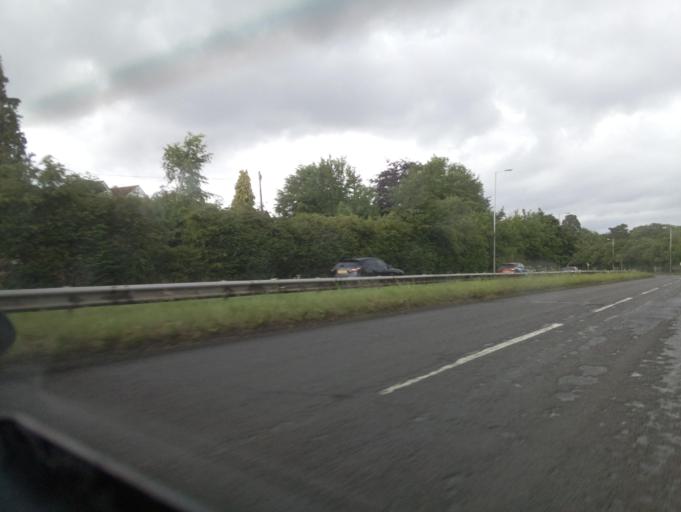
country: GB
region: England
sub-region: Dudley
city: Kingswinford
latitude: 52.5465
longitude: -2.1714
